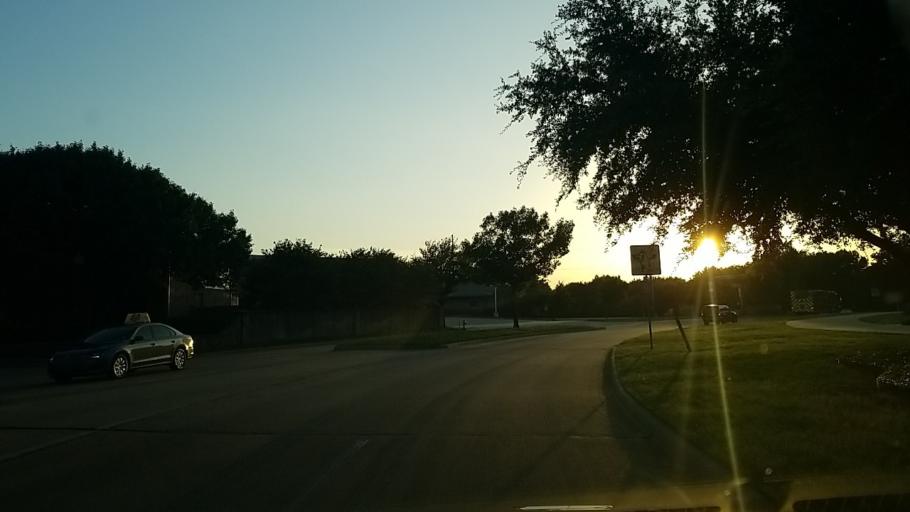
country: US
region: Texas
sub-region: Denton County
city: Highland Village
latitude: 33.0843
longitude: -97.0532
